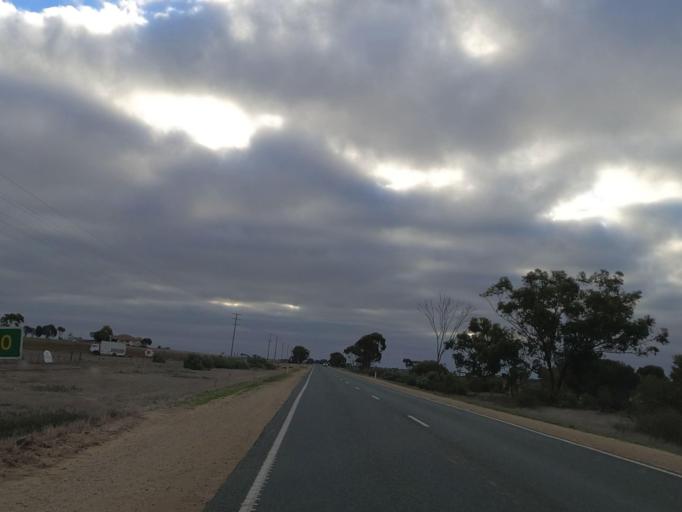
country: AU
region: Victoria
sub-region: Swan Hill
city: Swan Hill
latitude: -35.6431
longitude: 143.8314
